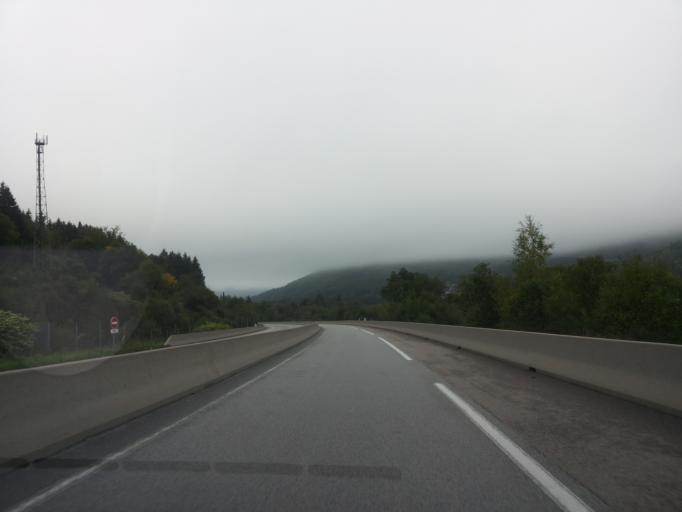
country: FR
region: Lorraine
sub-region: Departement des Vosges
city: Rupt-sur-Moselle
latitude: 47.9265
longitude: 6.6510
